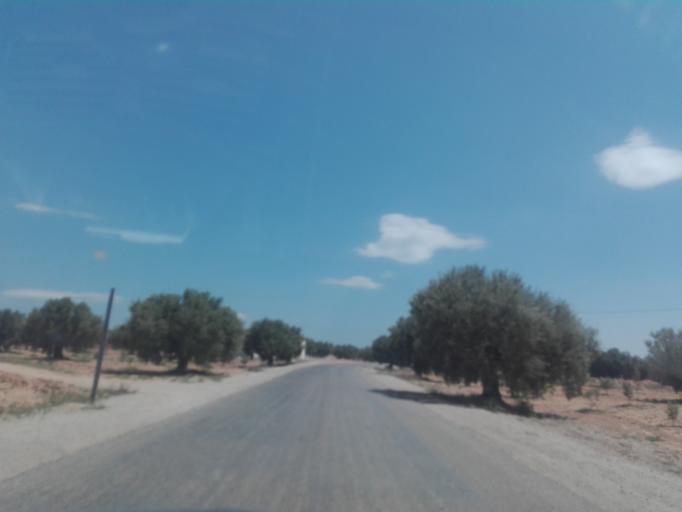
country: TN
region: Safaqis
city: Sfax
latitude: 34.6227
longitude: 10.6093
